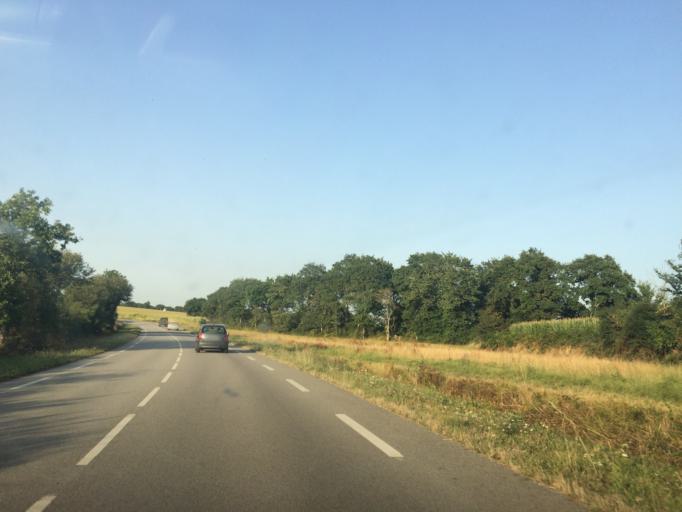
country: FR
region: Brittany
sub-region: Departement du Morbihan
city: Ambon
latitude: 47.5382
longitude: -2.5374
